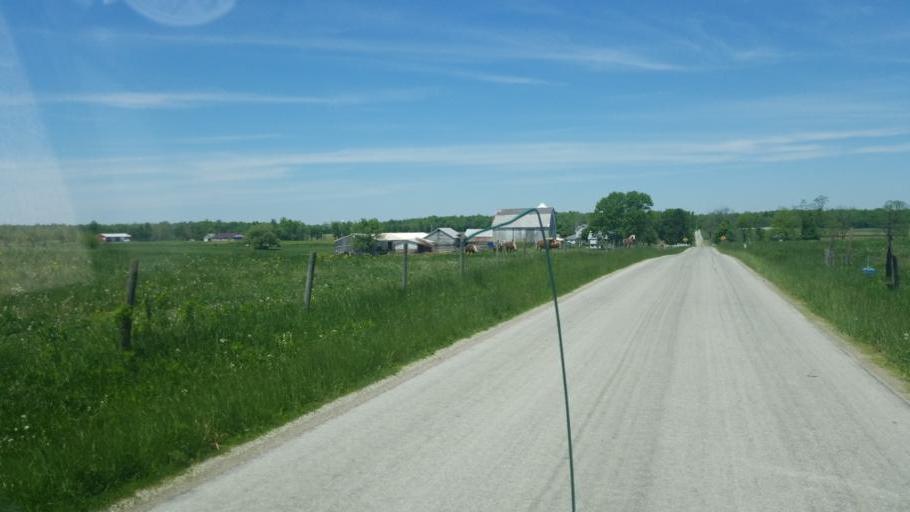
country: US
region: Ohio
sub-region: Huron County
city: Greenwich
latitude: 40.9719
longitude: -82.4318
